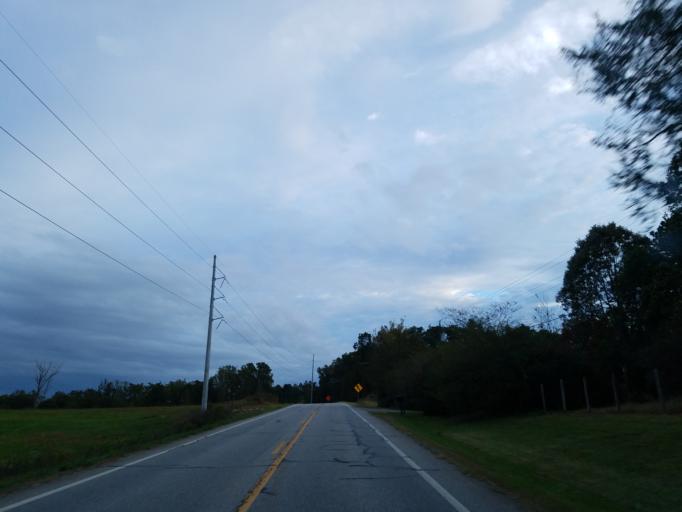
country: US
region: Georgia
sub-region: Dawson County
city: Dawsonville
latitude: 34.4366
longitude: -84.1632
